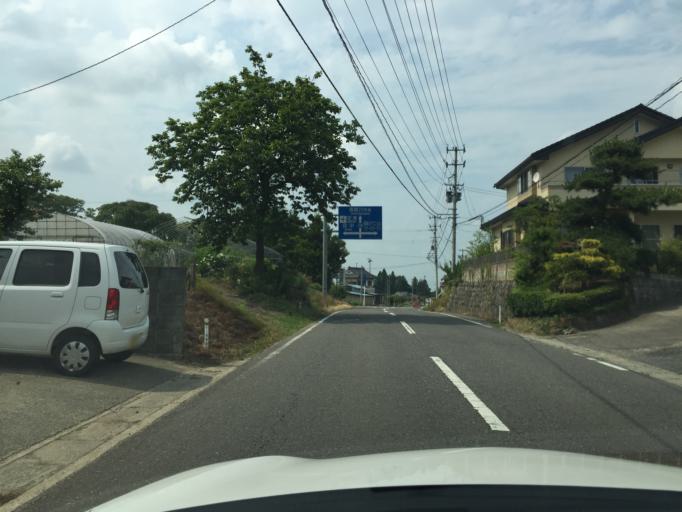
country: JP
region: Fukushima
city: Sukagawa
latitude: 37.2554
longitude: 140.4288
